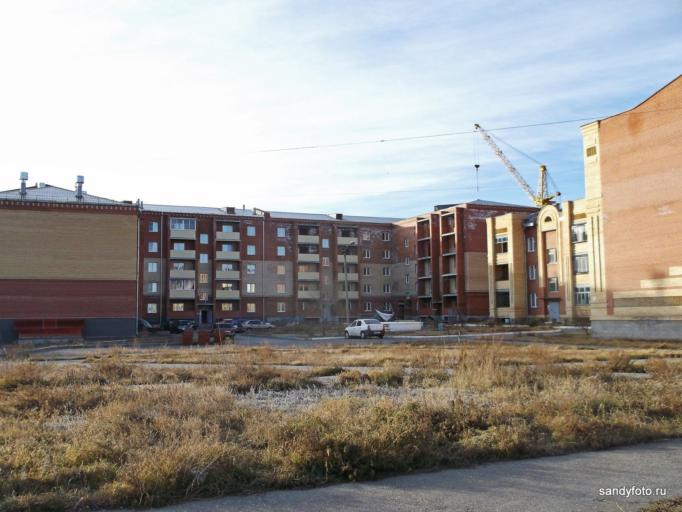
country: RU
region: Chelyabinsk
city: Troitsk
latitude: 54.0762
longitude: 61.5394
